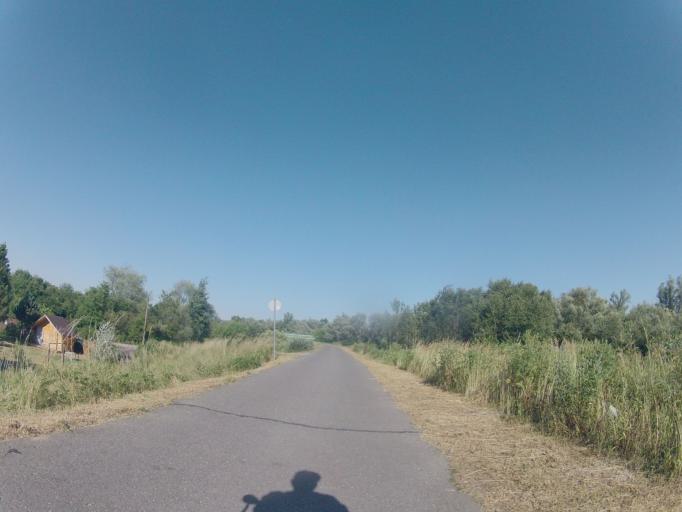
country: PL
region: Lesser Poland Voivodeship
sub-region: Krakow
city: Krakow
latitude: 50.0400
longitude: 19.8892
